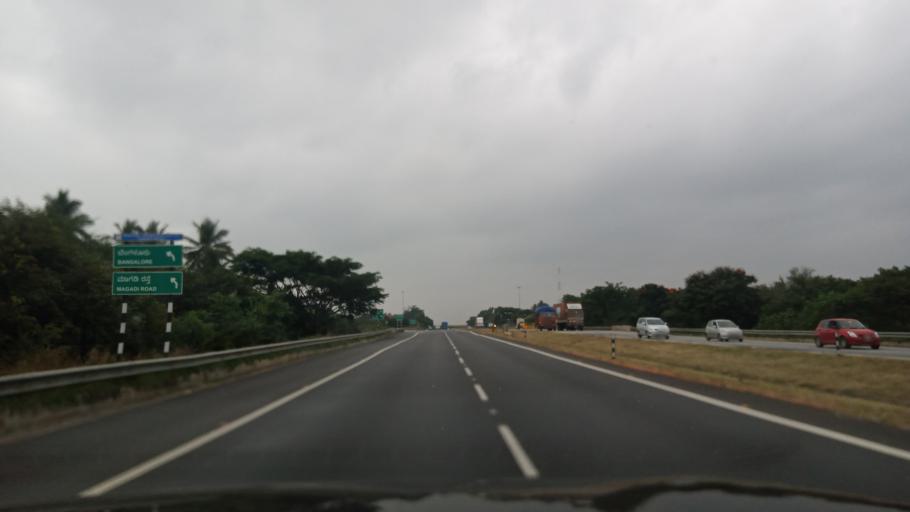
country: IN
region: Karnataka
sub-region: Bangalore Urban
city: Bangalore
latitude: 12.9945
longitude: 77.4734
